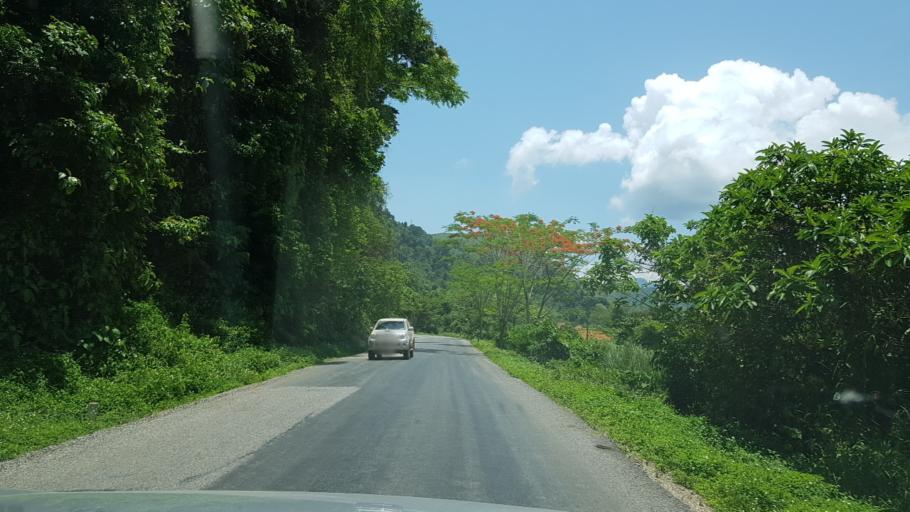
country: LA
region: Vientiane
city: Muang Kasi
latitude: 19.1244
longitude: 102.2605
